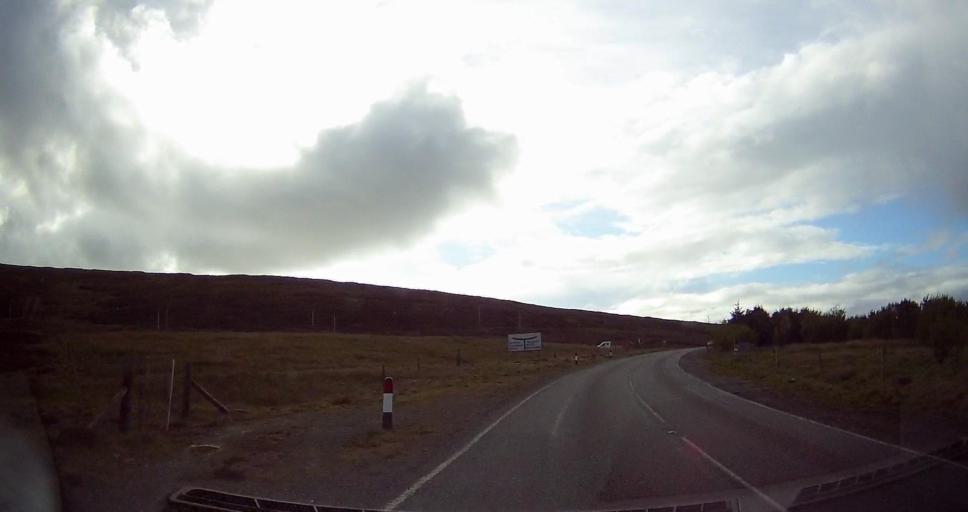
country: GB
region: Scotland
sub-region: Shetland Islands
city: Lerwick
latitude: 60.3441
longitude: -1.2500
